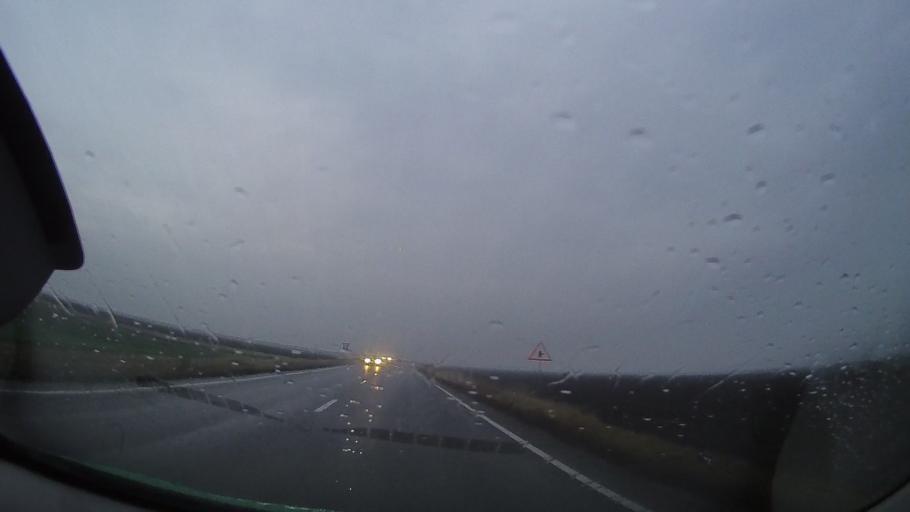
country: RO
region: Harghita
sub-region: Municipiul Gheorgheni
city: Gheorgheni
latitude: 46.7297
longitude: 25.5767
